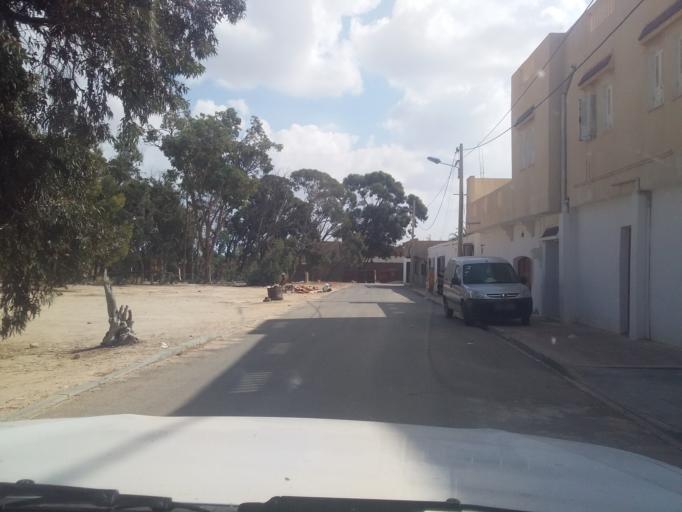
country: TN
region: Qabis
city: Gabes
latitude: 33.6222
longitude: 10.2808
